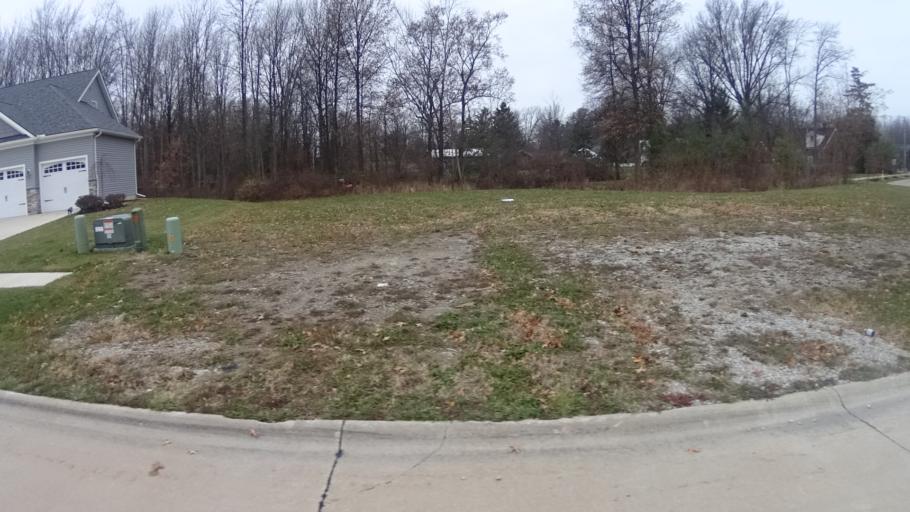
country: US
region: Ohio
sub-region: Lorain County
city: North Ridgeville
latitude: 41.3702
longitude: -81.9775
